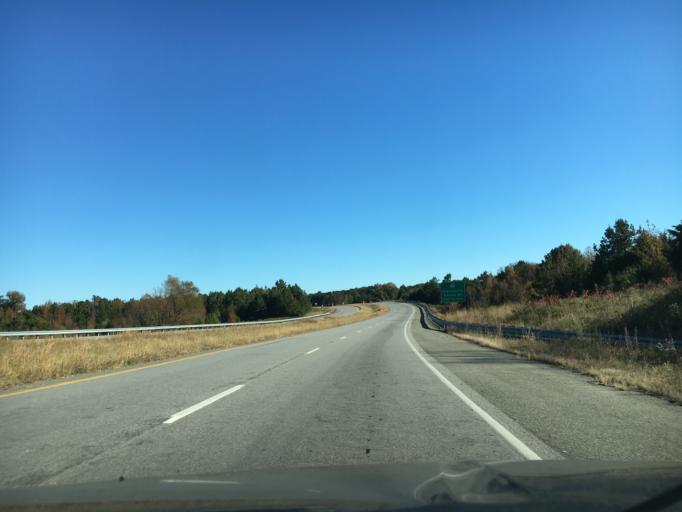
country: US
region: Virginia
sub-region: Mecklenburg County
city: Clarksville
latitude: 36.6095
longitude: -78.5780
